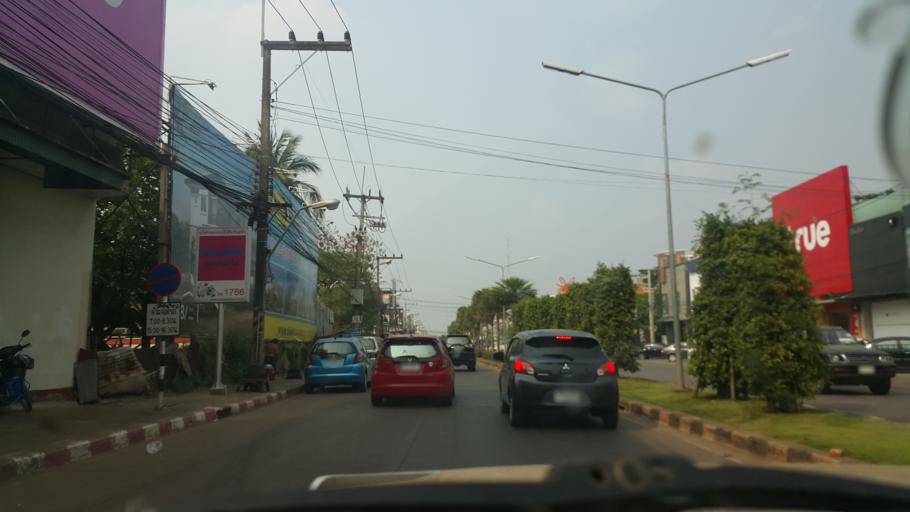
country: TH
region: Changwat Udon Thani
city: Udon Thani
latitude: 17.3992
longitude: 102.8042
